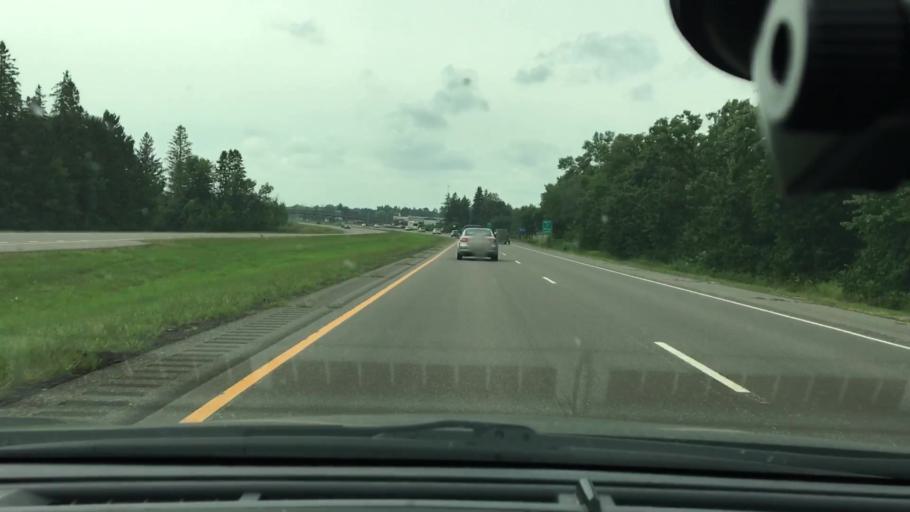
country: US
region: Minnesota
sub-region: Mille Lacs County
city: Vineland
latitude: 46.0770
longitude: -93.6549
